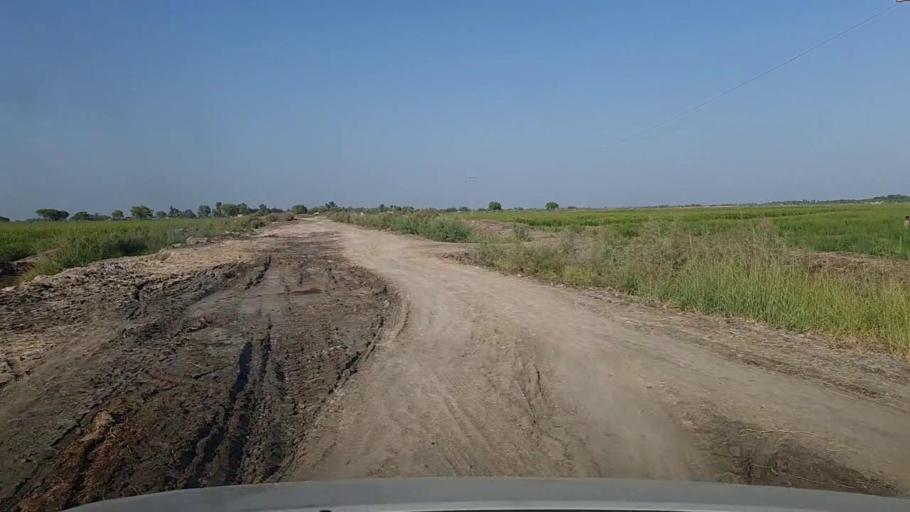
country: PK
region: Sindh
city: Kandhkot
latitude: 28.2755
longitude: 69.3158
